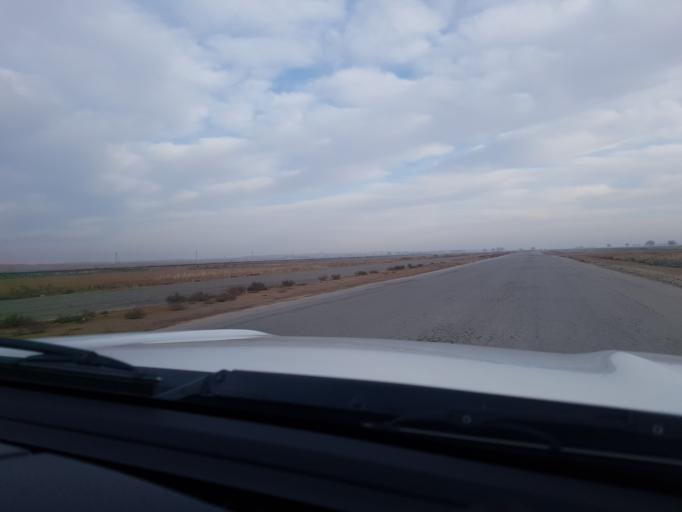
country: TM
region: Ahal
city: Abadan
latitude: 38.6343
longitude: 58.4986
